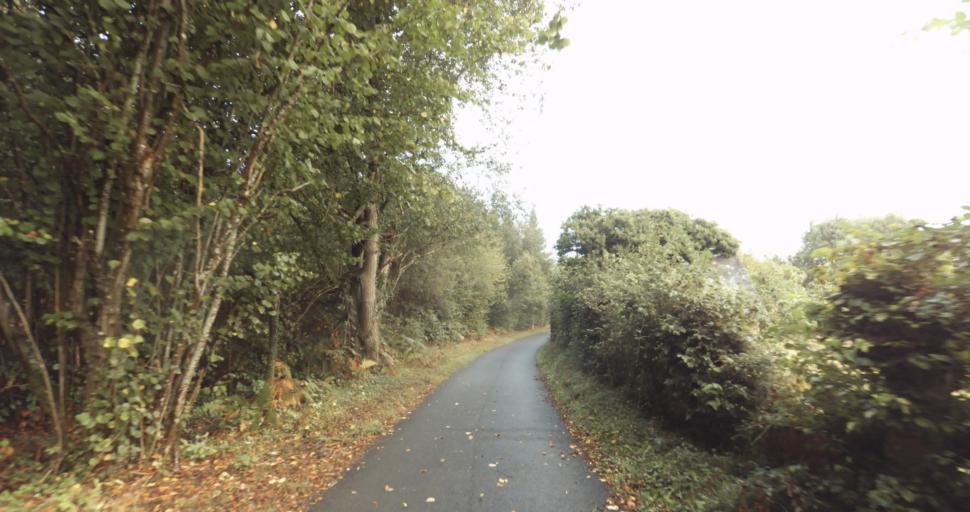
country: FR
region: Lower Normandy
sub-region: Departement de l'Orne
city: Vimoutiers
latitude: 48.8990
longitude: 0.2508
